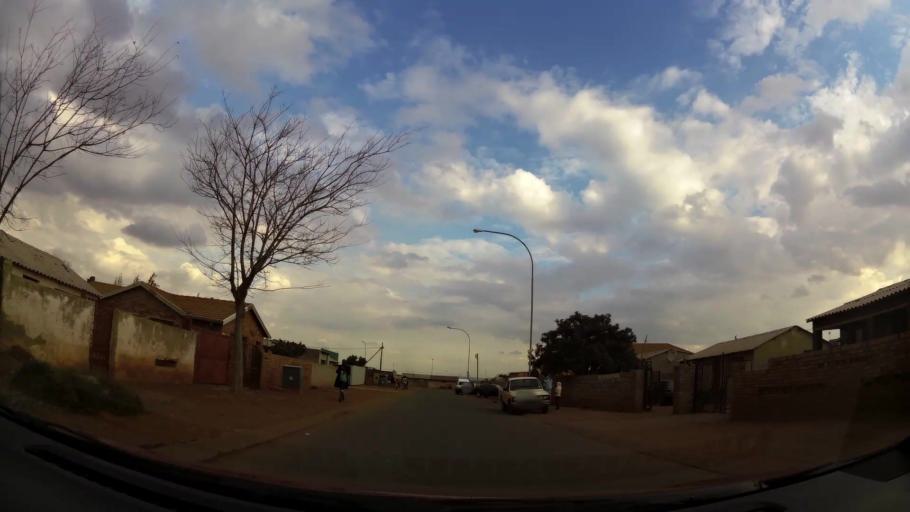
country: ZA
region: Gauteng
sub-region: City of Johannesburg Metropolitan Municipality
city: Soweto
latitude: -26.2442
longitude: 27.8159
